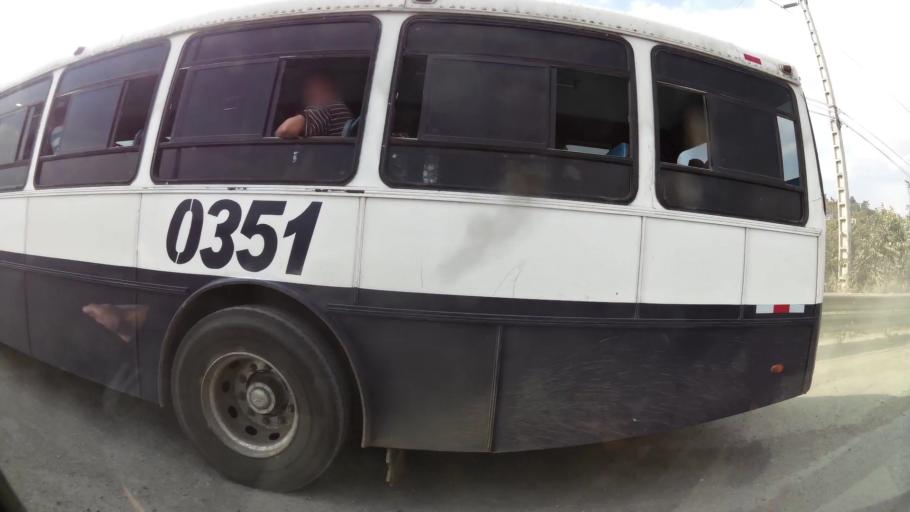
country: EC
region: Guayas
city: Santa Lucia
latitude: -2.1204
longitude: -79.9748
